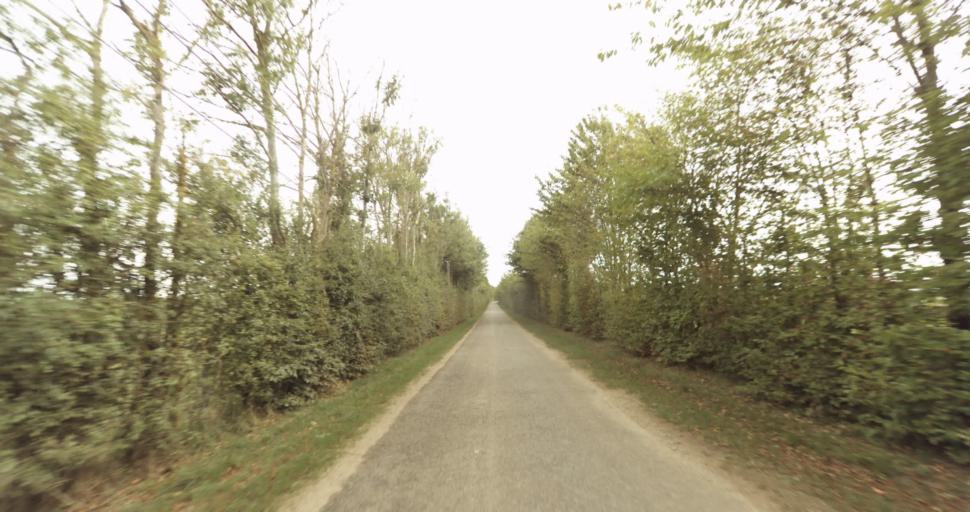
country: FR
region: Lower Normandy
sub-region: Departement de l'Orne
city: Sainte-Gauburge-Sainte-Colombe
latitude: 48.7348
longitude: 0.3650
